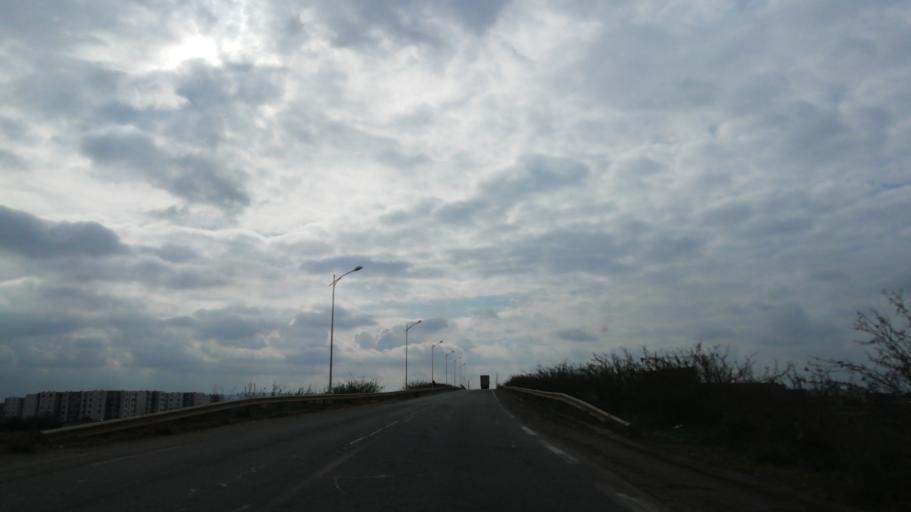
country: DZ
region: Oran
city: Sidi ech Chahmi
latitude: 35.5628
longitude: -0.4466
